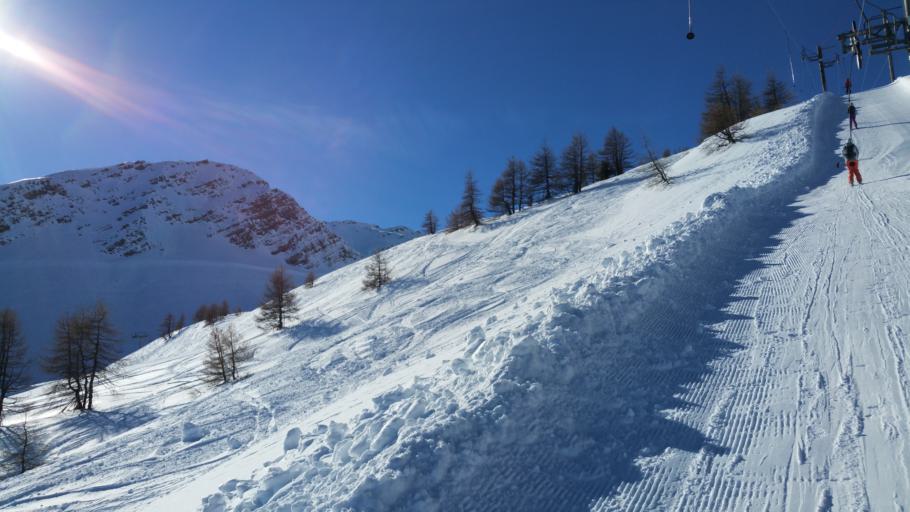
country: FR
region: Rhone-Alpes
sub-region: Departement de la Savoie
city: Villargondran
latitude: 45.2169
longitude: 6.3940
